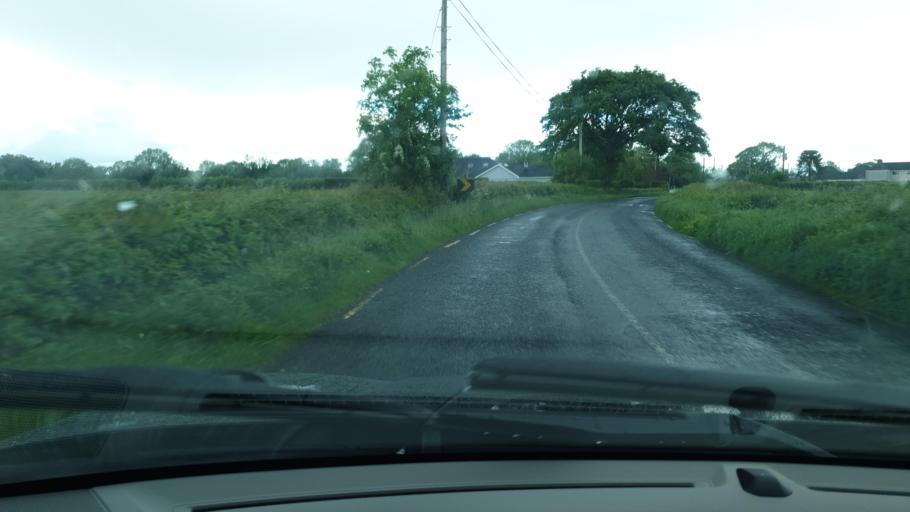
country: IE
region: Leinster
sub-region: Laois
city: Mountmellick
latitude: 53.1077
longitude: -7.3894
